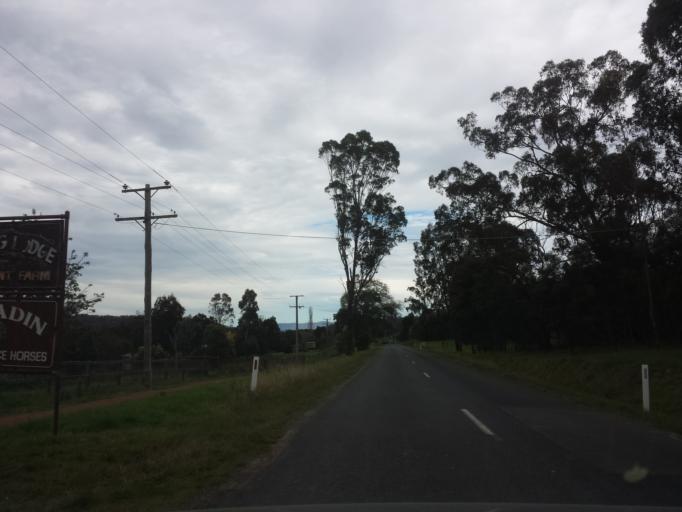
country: AU
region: Victoria
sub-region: Yarra Ranges
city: Yarra Glen
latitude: -37.5972
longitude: 145.3730
